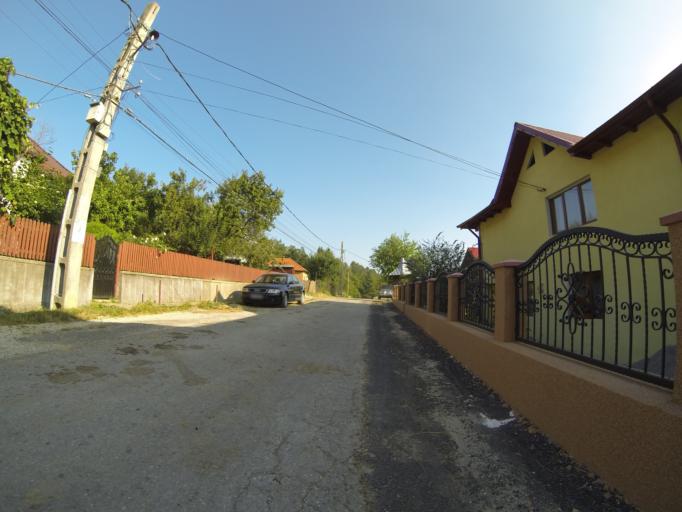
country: RO
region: Valcea
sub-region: Comuna Horezu
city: Horezu
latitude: 45.1802
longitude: 23.9926
